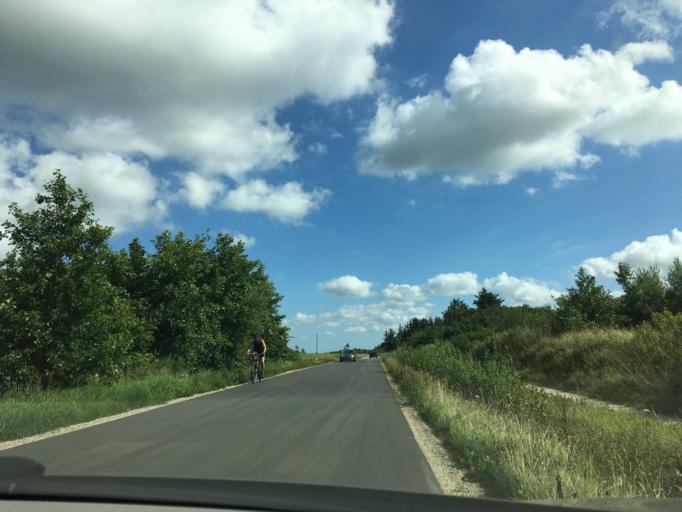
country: DK
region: South Denmark
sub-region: Varde Kommune
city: Oksbol
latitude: 55.8387
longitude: 8.2680
